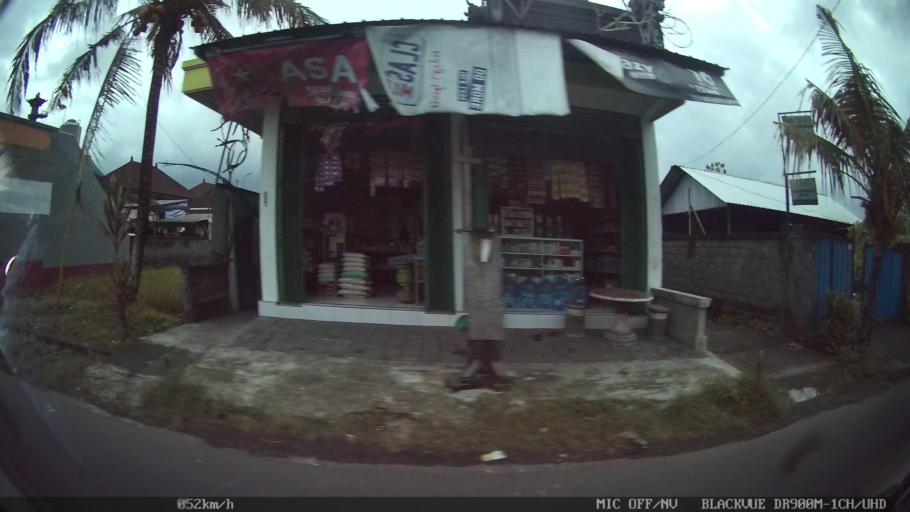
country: ID
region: Bali
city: Banjar Serangan
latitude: -8.5544
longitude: 115.1804
